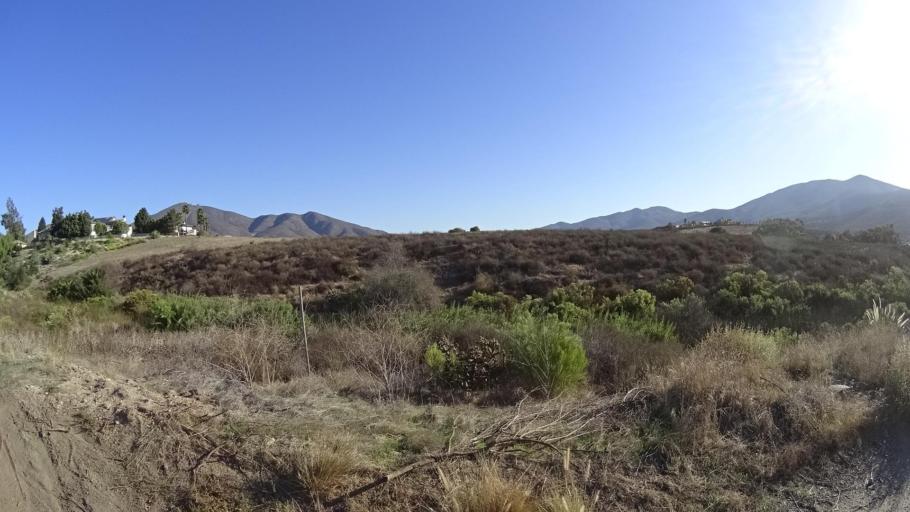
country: US
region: California
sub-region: San Diego County
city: La Presa
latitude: 32.6590
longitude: -116.9405
